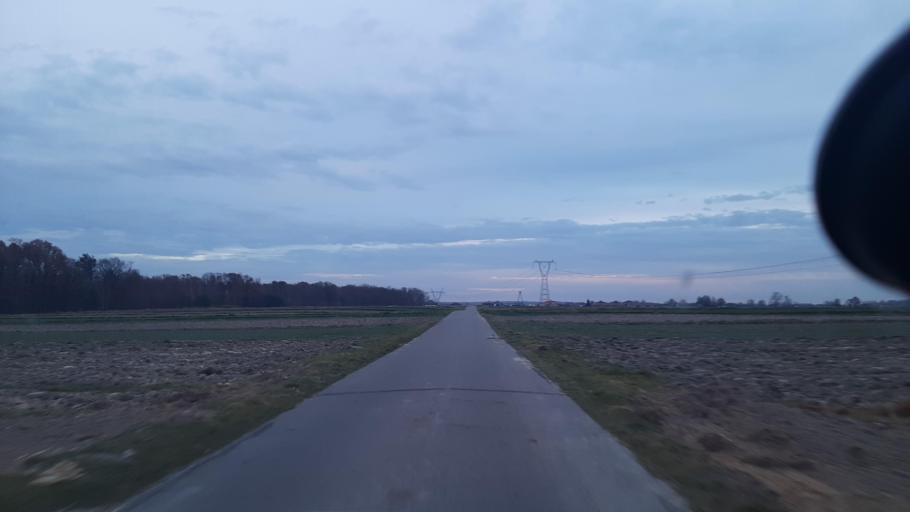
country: PL
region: Lublin Voivodeship
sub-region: Powiat lubelski
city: Garbow
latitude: 51.3737
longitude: 22.3762
